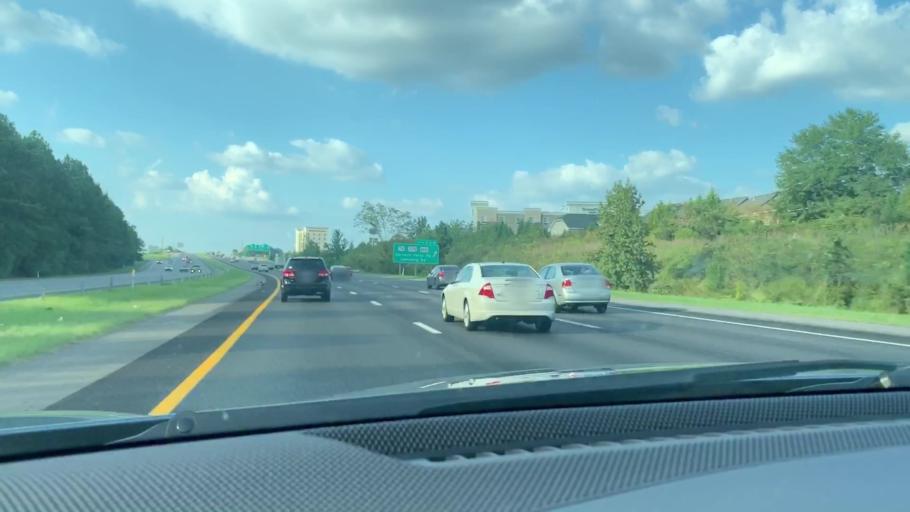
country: US
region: South Carolina
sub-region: Richland County
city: Forest Acres
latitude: 33.9649
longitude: -80.9529
